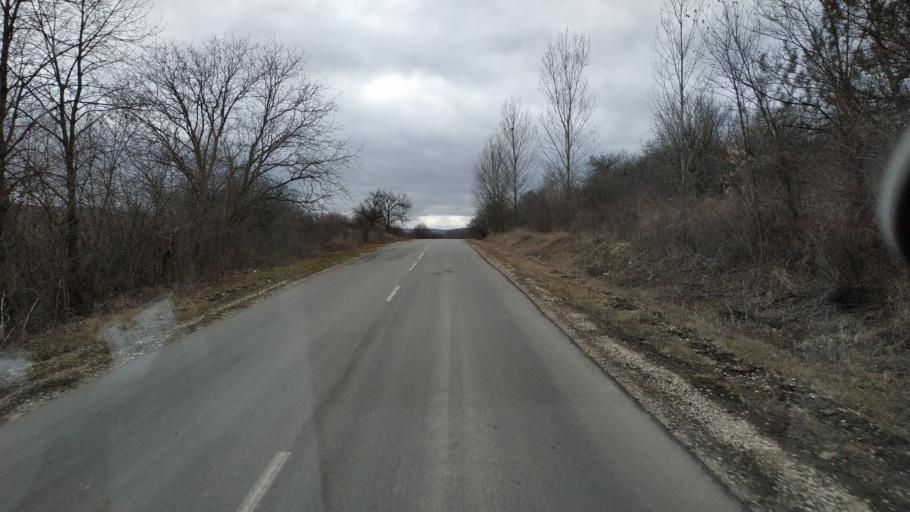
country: MD
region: Calarasi
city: Calarasi
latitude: 47.2395
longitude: 28.1750
